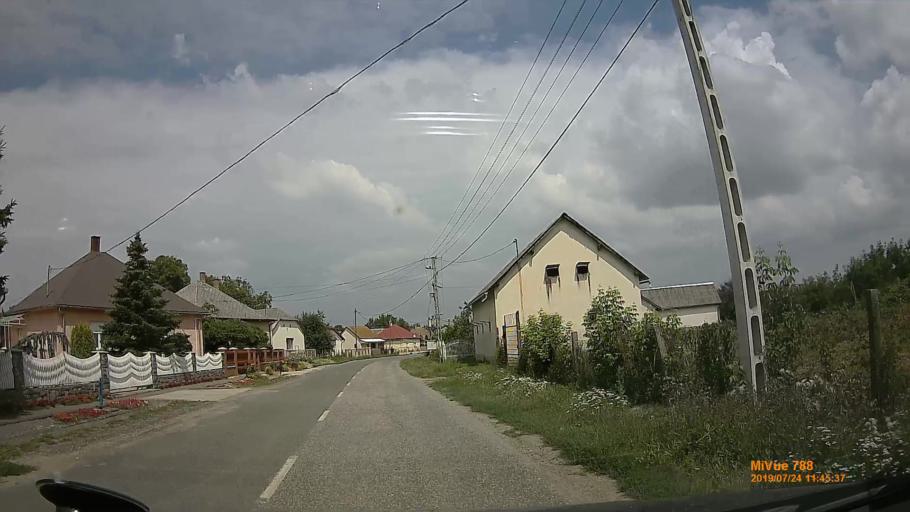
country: UA
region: Zakarpattia
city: Batiovo
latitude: 48.2333
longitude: 22.4327
